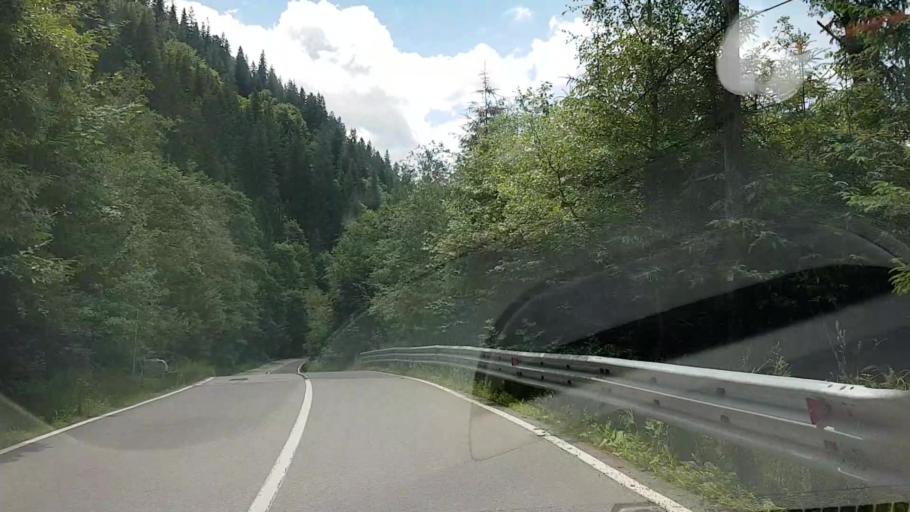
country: RO
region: Suceava
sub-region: Comuna Crucea
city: Crucea
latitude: 47.3797
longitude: 25.5878
